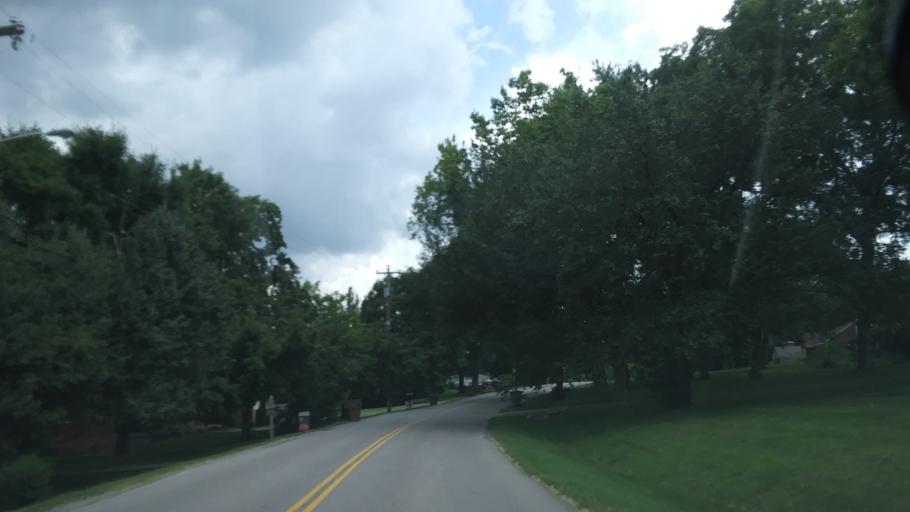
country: US
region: Tennessee
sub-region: Davidson County
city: Belle Meade
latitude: 36.1387
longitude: -86.8776
